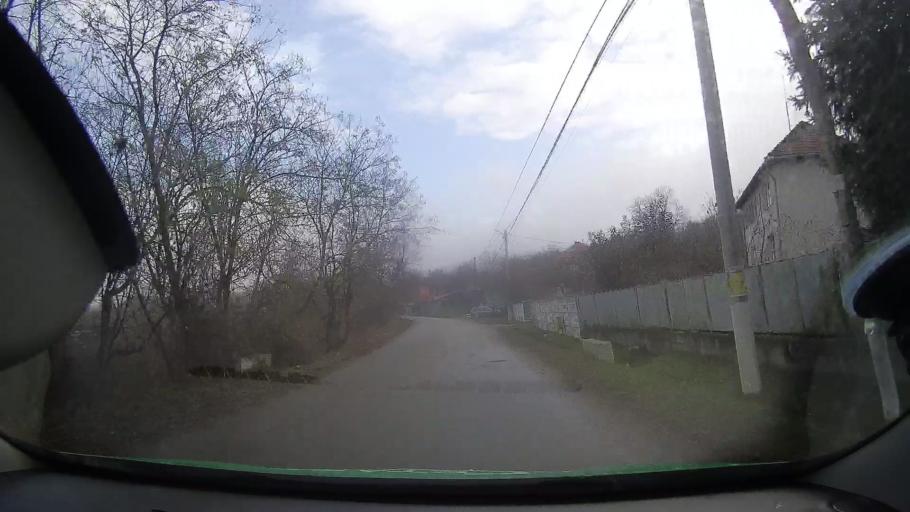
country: RO
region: Alba
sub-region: Comuna Noslac
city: Noslac
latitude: 46.4204
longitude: 23.9853
